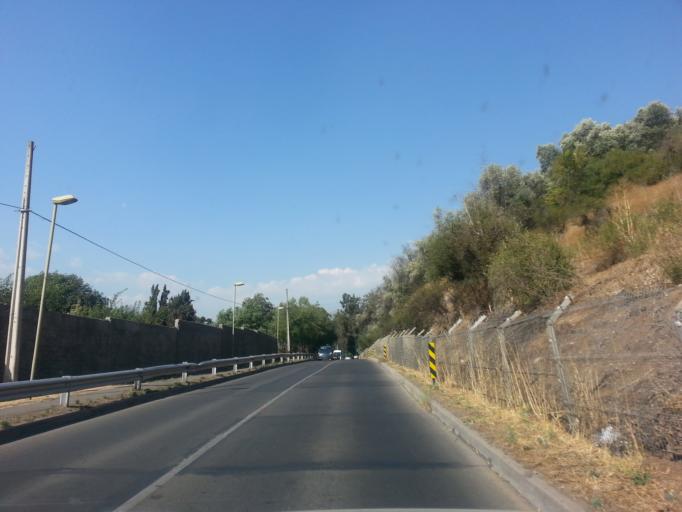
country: CL
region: Santiago Metropolitan
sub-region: Provincia de Santiago
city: Villa Presidente Frei, Nunoa, Santiago, Chile
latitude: -33.3826
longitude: -70.5145
